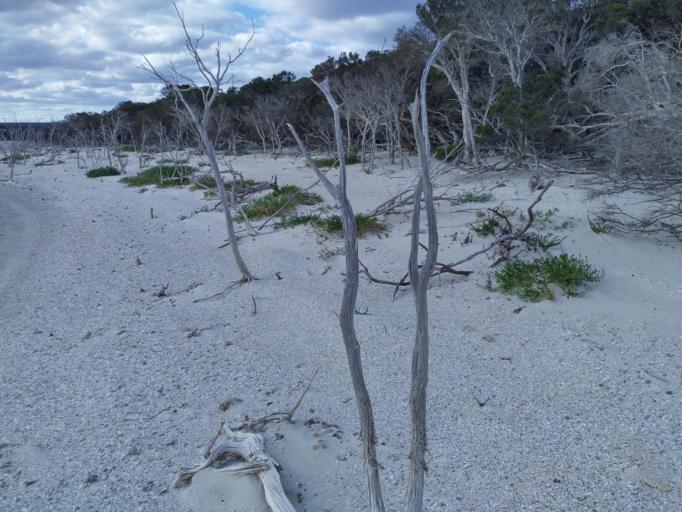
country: AU
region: Western Australia
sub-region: Ravensthorpe
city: Ravensthorpe
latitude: -33.9609
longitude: 119.9127
